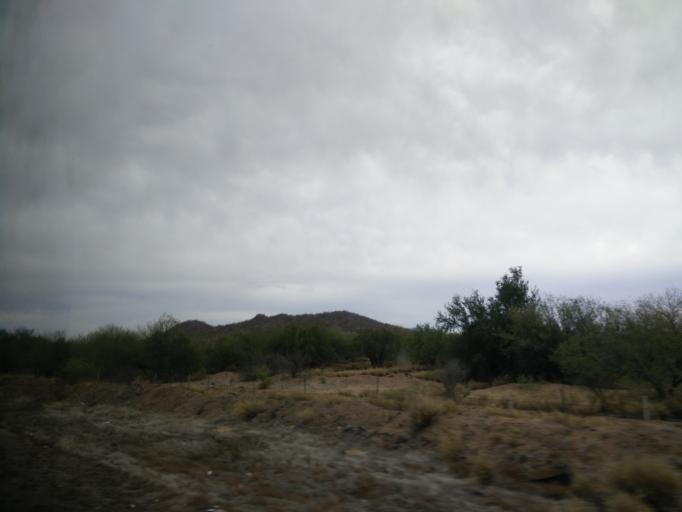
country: MX
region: Sonora
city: Hermosillo
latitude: 28.8415
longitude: -110.9582
